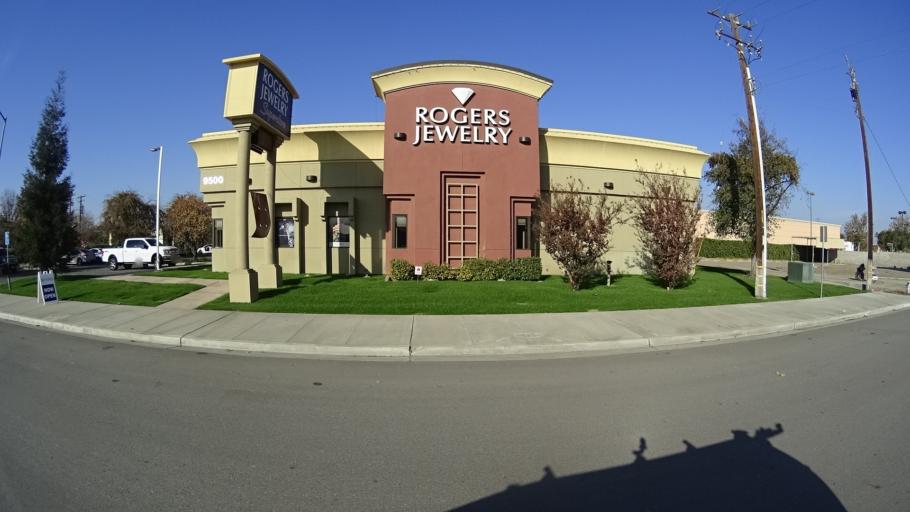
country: US
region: California
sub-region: Kern County
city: Greenacres
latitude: 35.3832
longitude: -119.1079
